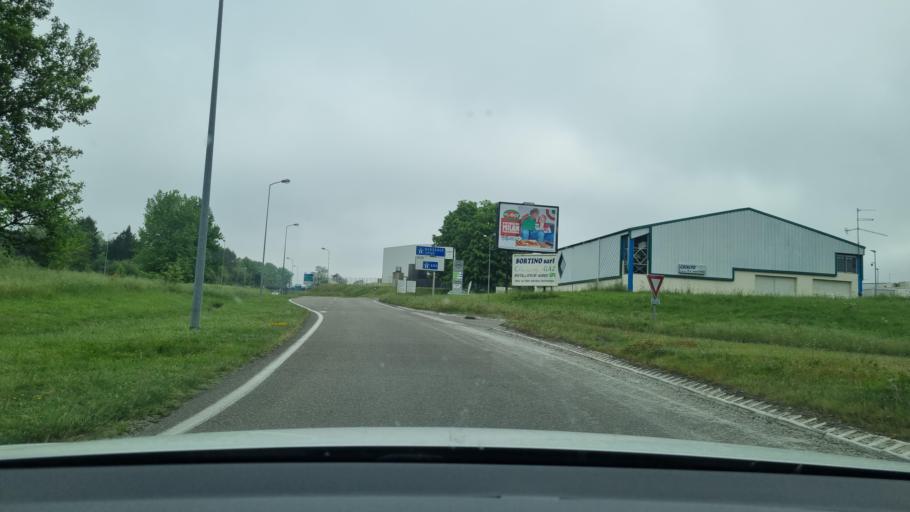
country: FR
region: Aquitaine
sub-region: Departement des Landes
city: Saint-Pierre-du-Mont
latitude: 43.8632
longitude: -0.5140
